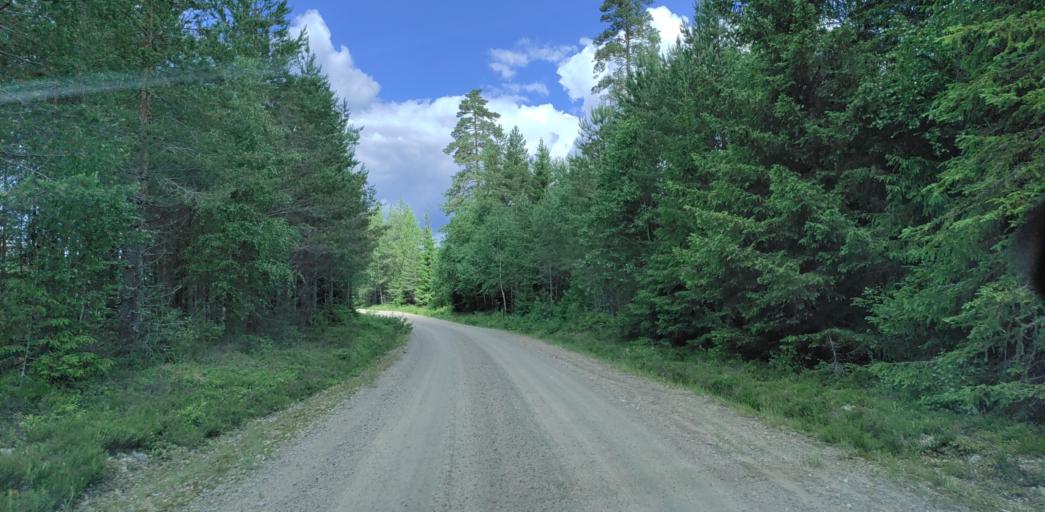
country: SE
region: Vaermland
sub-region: Hagfors Kommun
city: Ekshaerad
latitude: 60.0711
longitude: 13.2908
